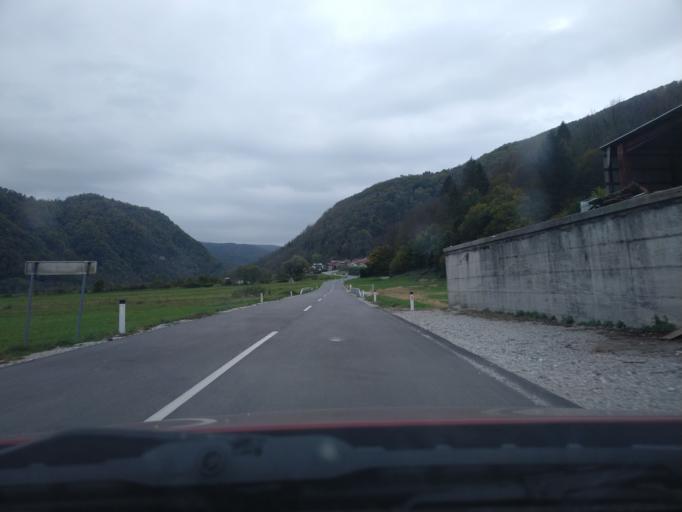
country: SI
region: Tolmin
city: Tolmin
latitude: 46.1688
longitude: 13.7092
